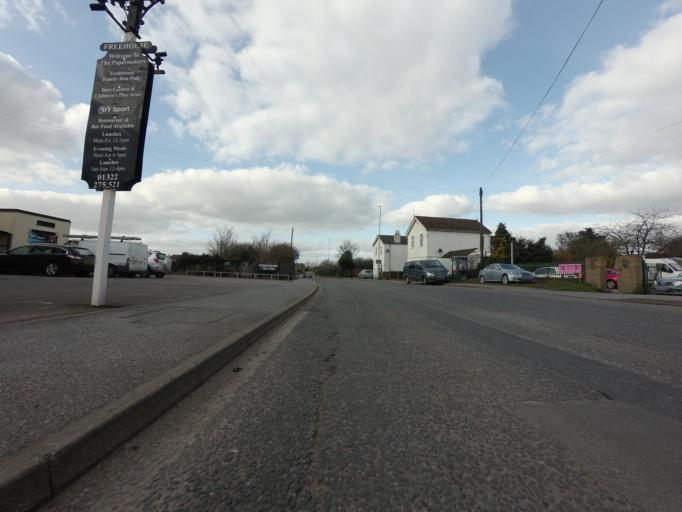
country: GB
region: England
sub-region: Kent
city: Dartford
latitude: 51.4214
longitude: 0.2315
